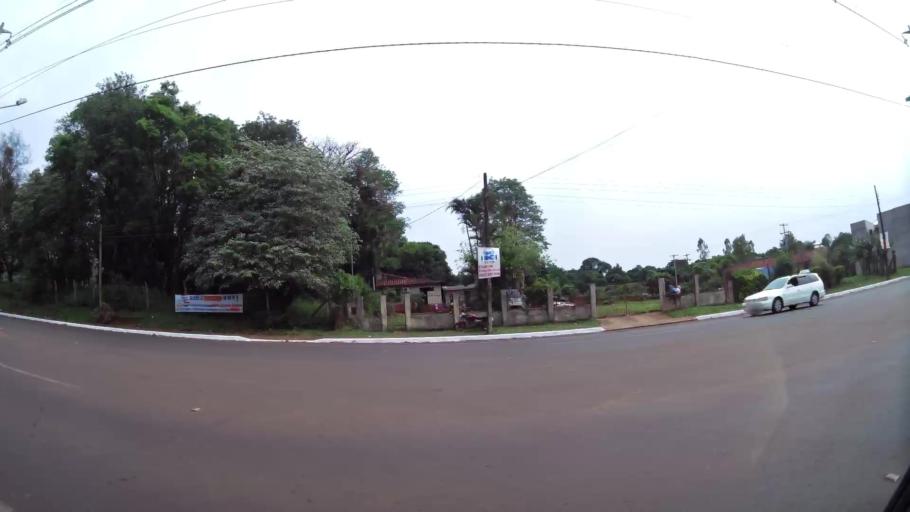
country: PY
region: Alto Parana
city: Presidente Franco
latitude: -25.5482
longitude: -54.6187
